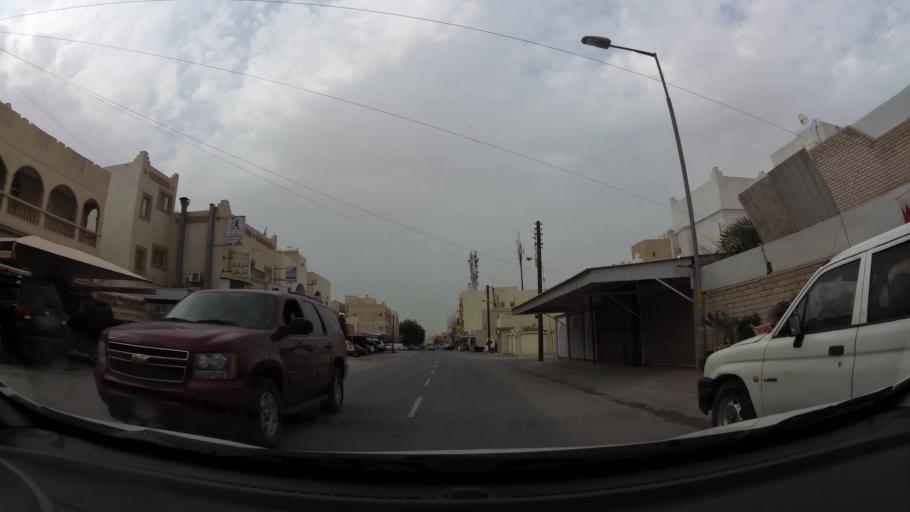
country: BH
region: Northern
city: Ar Rifa'
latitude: 26.1249
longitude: 50.5791
